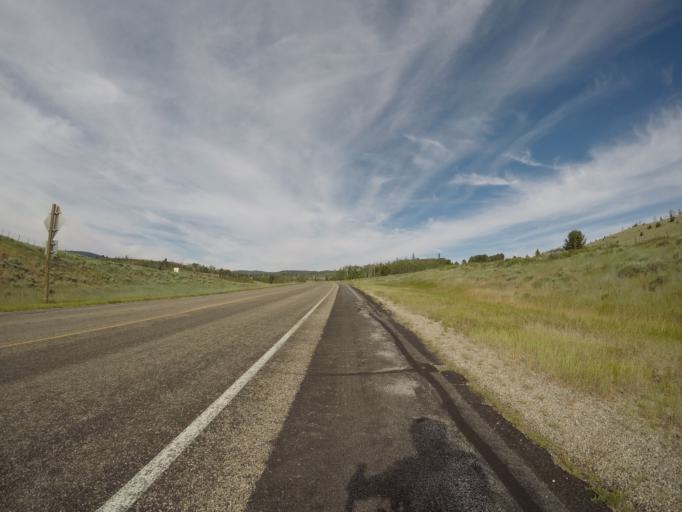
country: US
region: Wyoming
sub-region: Carbon County
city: Saratoga
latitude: 41.1808
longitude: -106.8756
